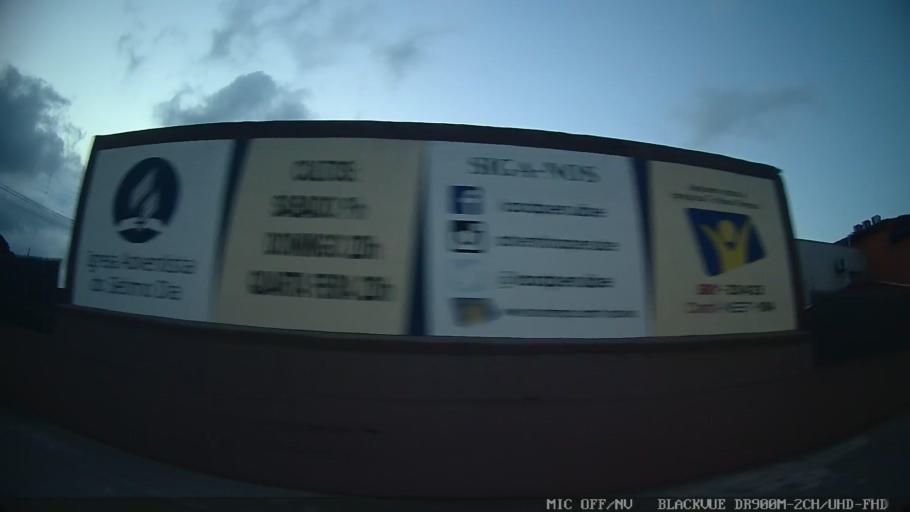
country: BR
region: Sao Paulo
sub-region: Peruibe
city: Peruibe
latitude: -24.3205
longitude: -46.9987
